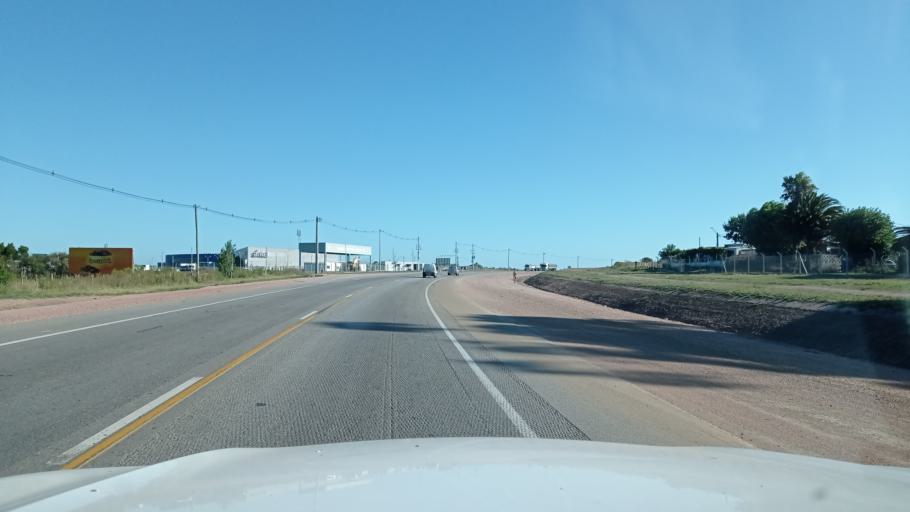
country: UY
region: Canelones
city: Pando
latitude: -34.7216
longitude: -55.9487
